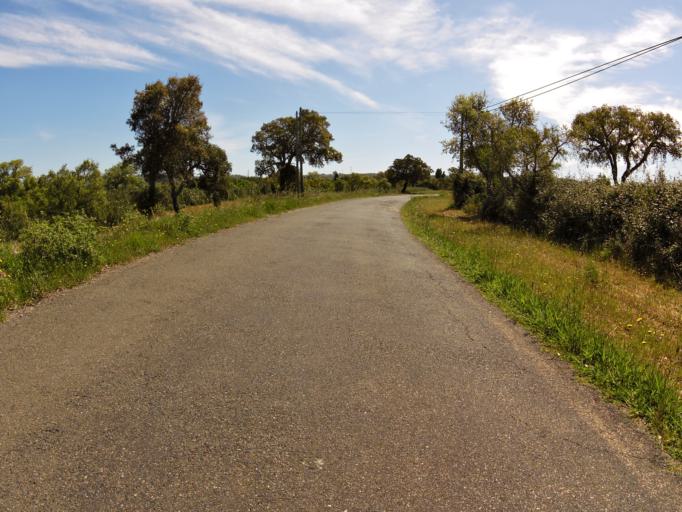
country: PT
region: Setubal
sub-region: Santiago do Cacem
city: Santiago do Cacem
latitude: 37.9399
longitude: -8.7437
